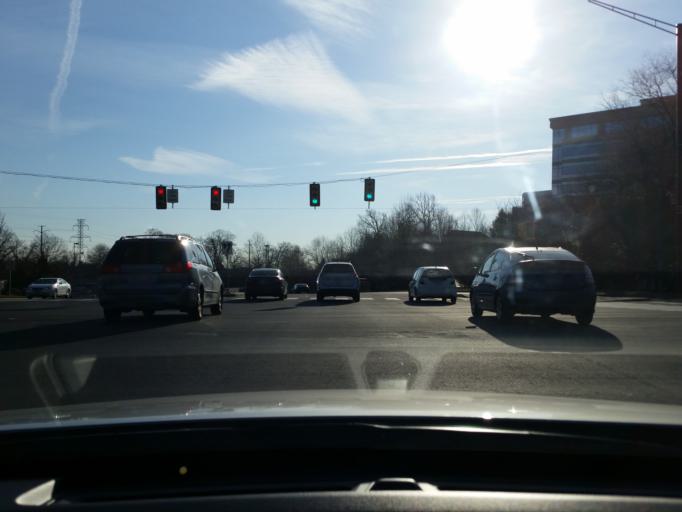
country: US
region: Virginia
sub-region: Fairfax County
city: Reston
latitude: 38.9552
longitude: -77.3557
